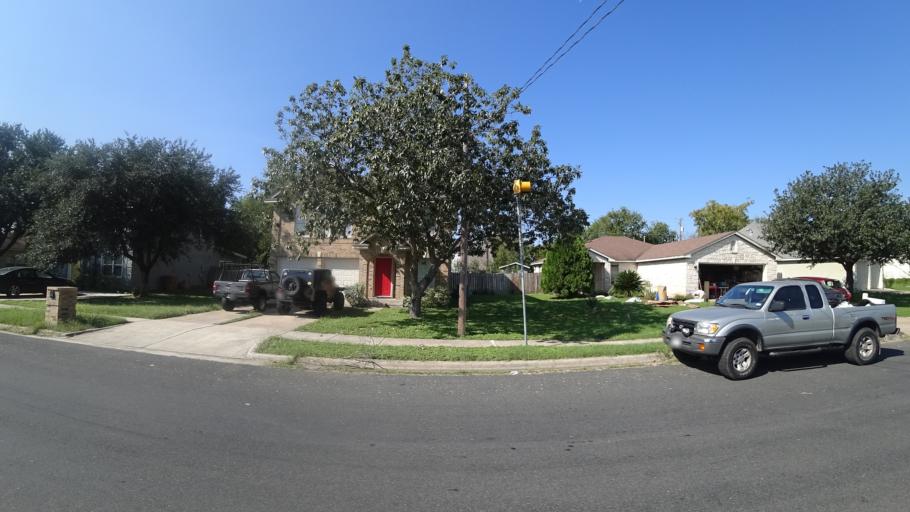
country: US
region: Texas
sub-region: Travis County
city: Austin
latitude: 30.3147
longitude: -97.6661
